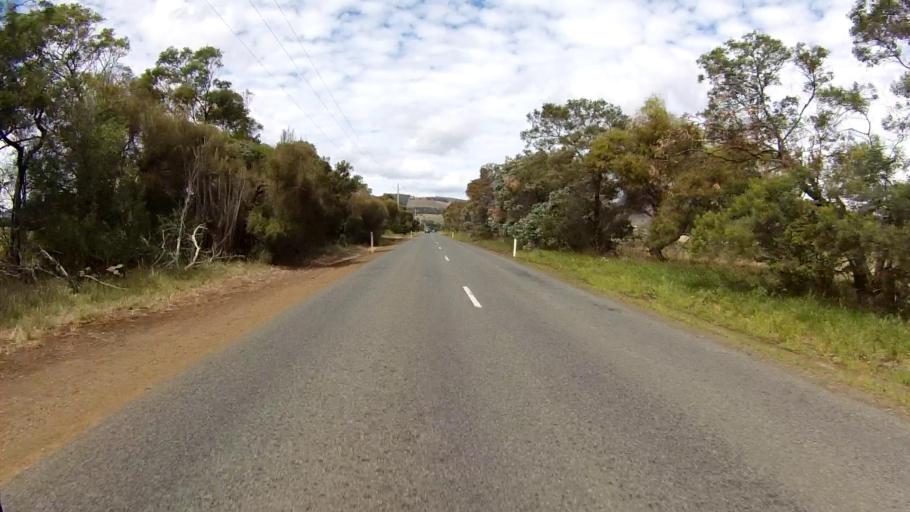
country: AU
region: Tasmania
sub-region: Clarence
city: Cambridge
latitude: -42.7527
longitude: 147.4091
